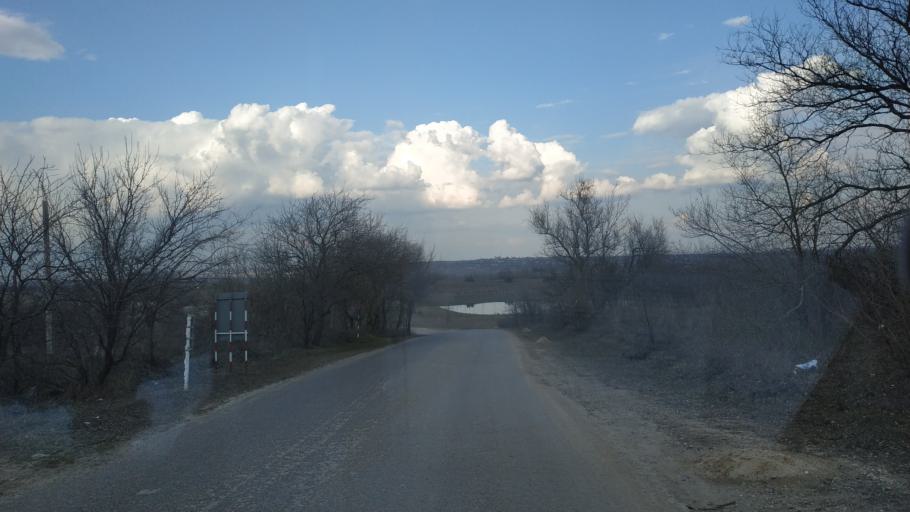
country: MD
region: Anenii Noi
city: Varnita
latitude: 46.9025
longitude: 29.4577
